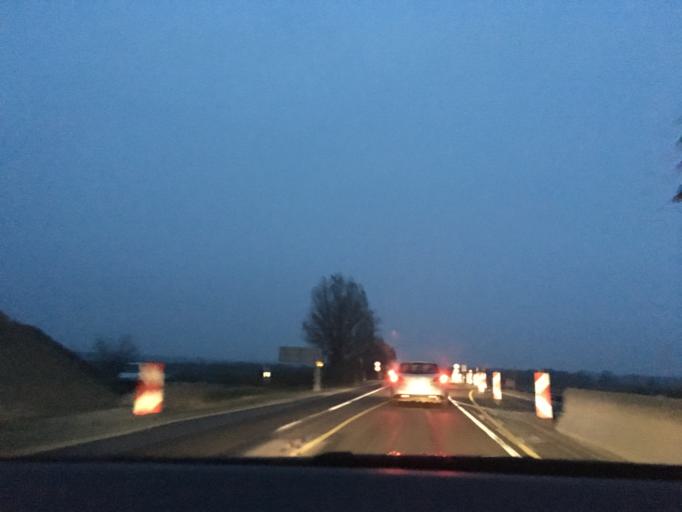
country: HU
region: Pest
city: Cegledbercel
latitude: 47.2220
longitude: 19.6942
